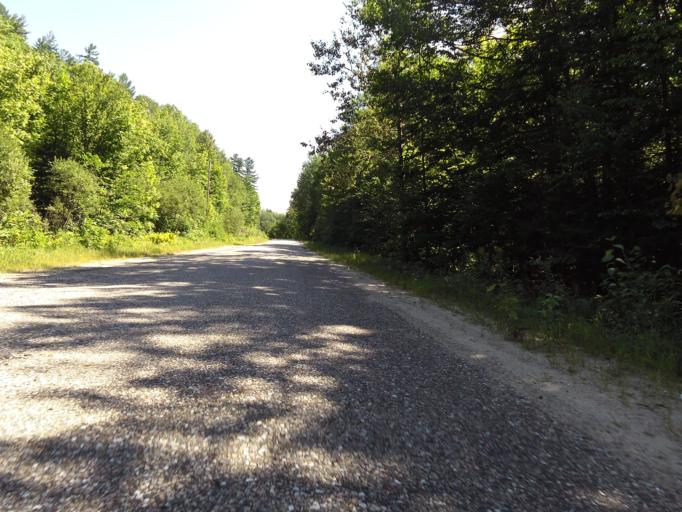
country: CA
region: Quebec
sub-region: Outaouais
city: Maniwaki
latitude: 46.2177
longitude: -76.0835
